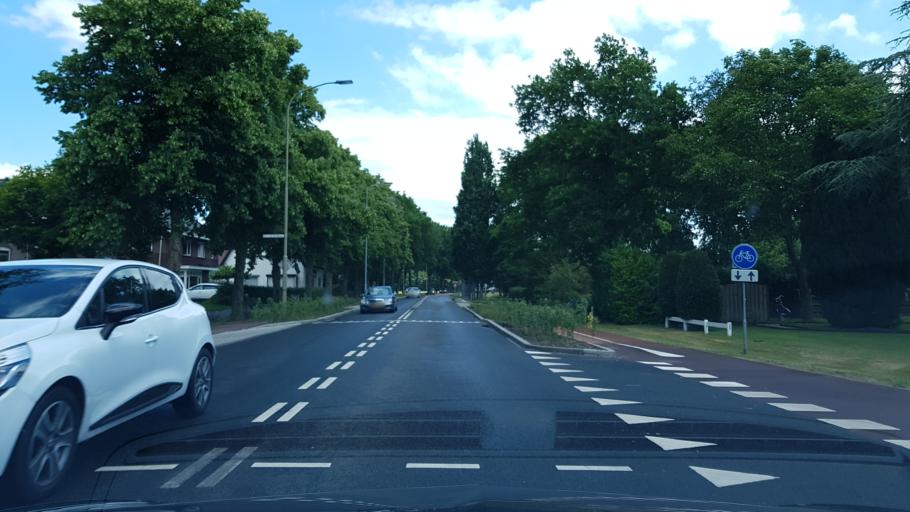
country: NL
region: Gelderland
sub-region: Gemeente Nunspeet
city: Nunspeet
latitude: 52.3648
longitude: 5.7348
